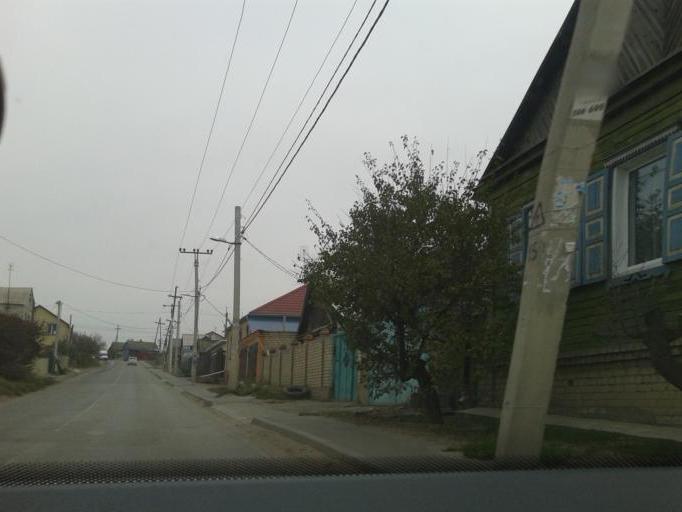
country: RU
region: Volgograd
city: Volgograd
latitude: 48.6964
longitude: 44.4479
